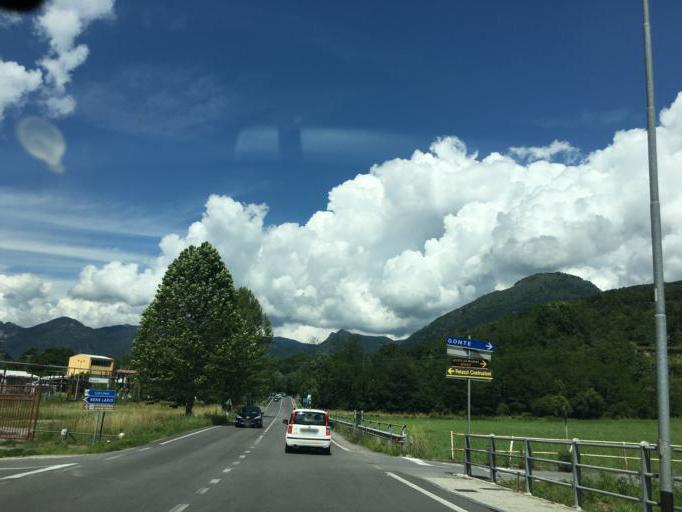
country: IT
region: Lombardy
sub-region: Provincia di Como
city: Codogna-Cardano
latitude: 46.0264
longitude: 9.2062
